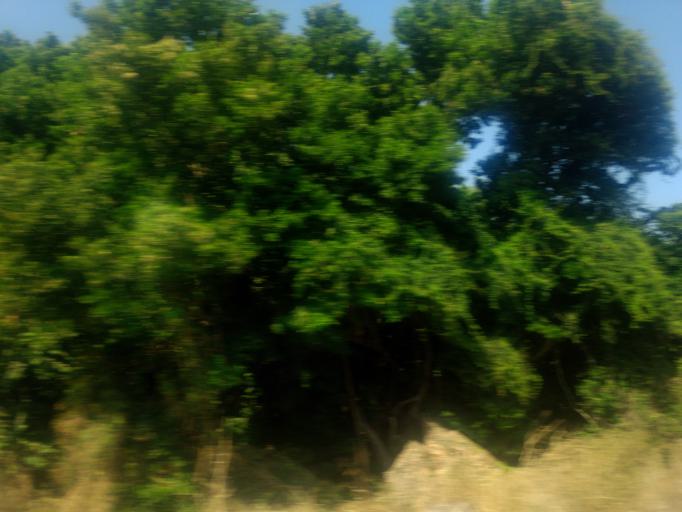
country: MX
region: Colima
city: El Colomo
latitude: 19.0351
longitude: -104.2554
